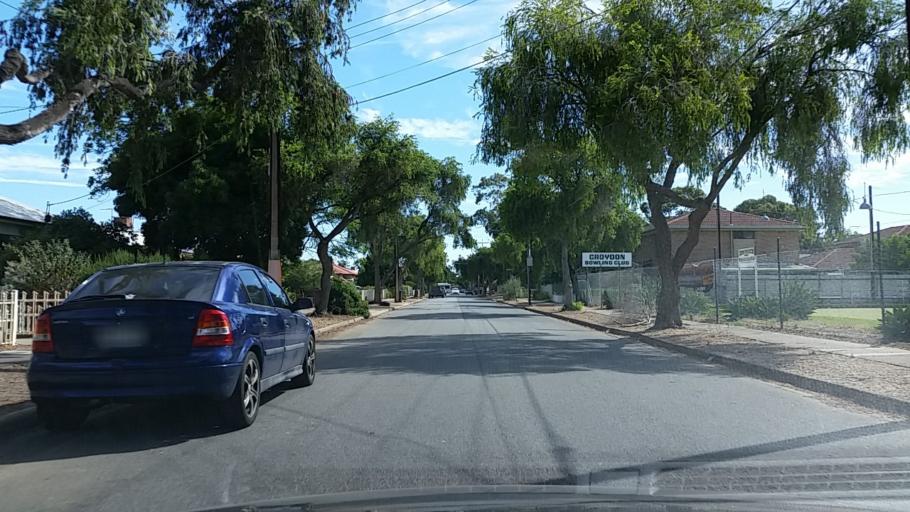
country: AU
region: South Australia
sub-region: Charles Sturt
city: Allenby Gardens
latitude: -34.8926
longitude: 138.5734
